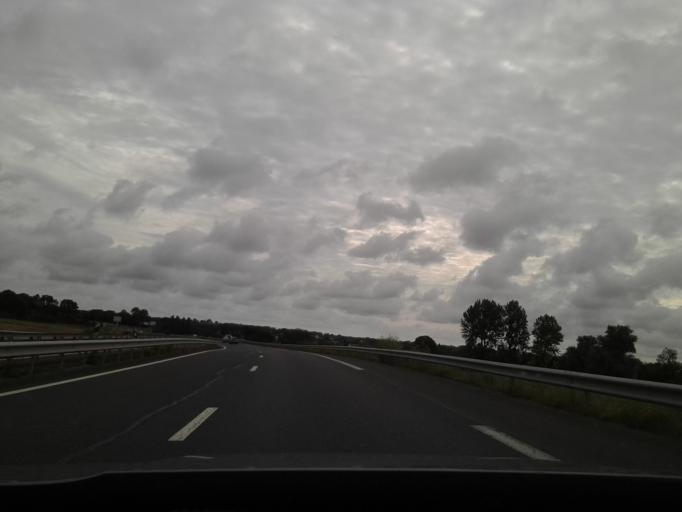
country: FR
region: Lower Normandy
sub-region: Departement du Calvados
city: Isigny-sur-Mer
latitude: 49.3255
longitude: -1.0817
